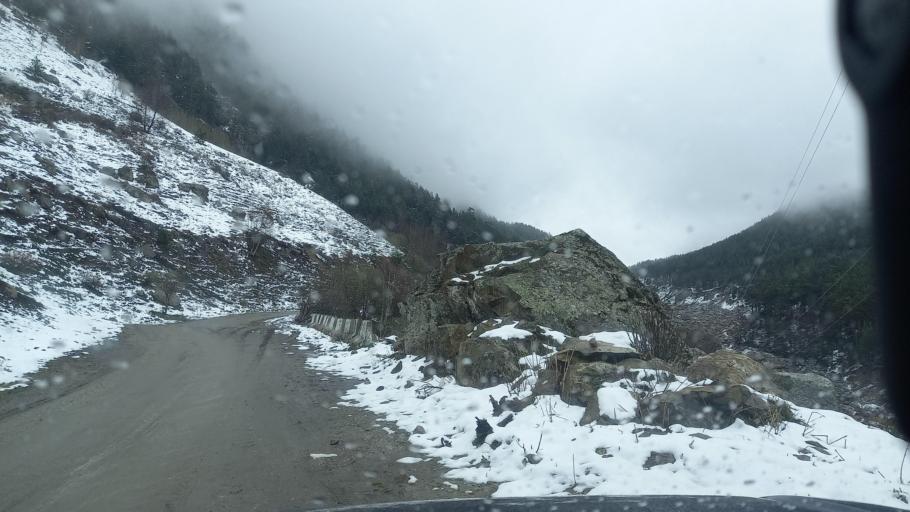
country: RU
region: Kabardino-Balkariya
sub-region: El'brusskiy Rayon
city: El'brus
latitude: 43.2243
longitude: 42.6770
